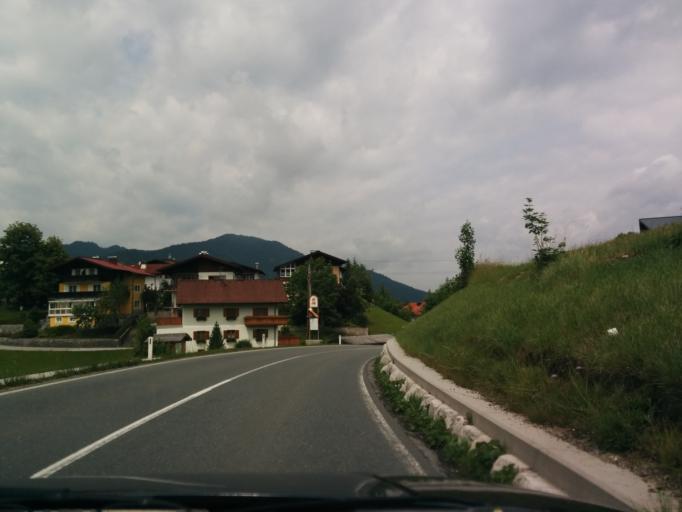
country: AT
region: Salzburg
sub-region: Politischer Bezirk Hallein
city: Abtenau
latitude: 47.5594
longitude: 13.3525
